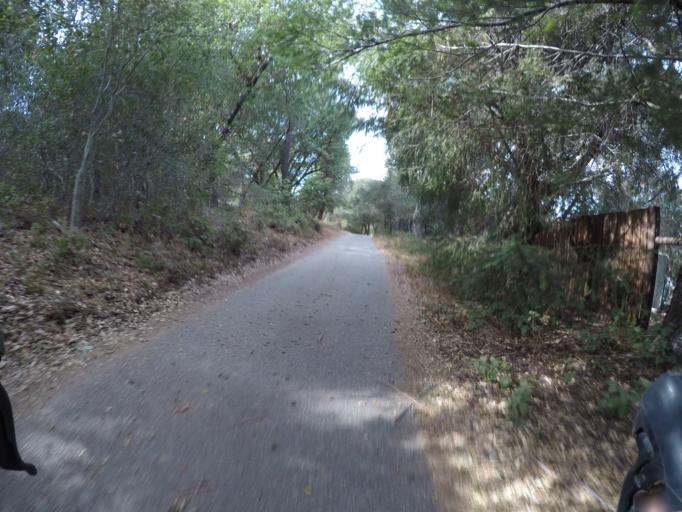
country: US
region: California
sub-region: Santa Cruz County
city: Mount Hermon
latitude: 37.0663
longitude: -122.0611
